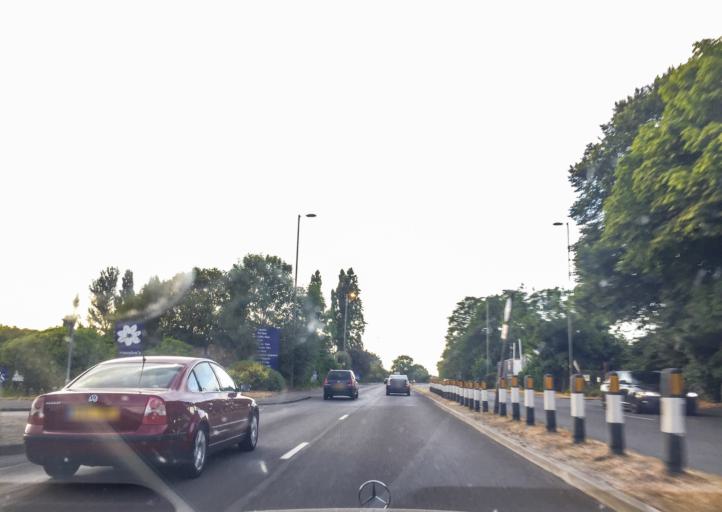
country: GB
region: England
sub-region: Surrey
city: Staines
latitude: 51.4593
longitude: -0.4939
